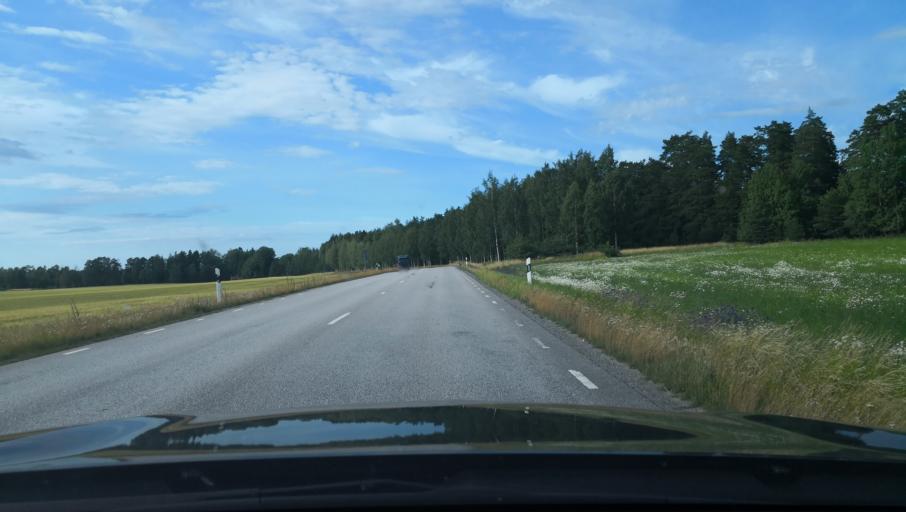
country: SE
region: Uppsala
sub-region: Habo Kommun
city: Balsta
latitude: 59.6195
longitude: 17.4976
